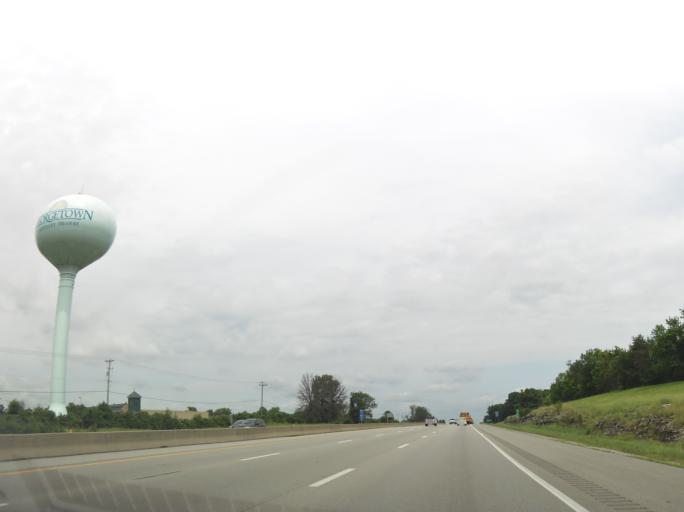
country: US
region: Kentucky
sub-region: Scott County
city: Georgetown
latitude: 38.2311
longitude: -84.5407
